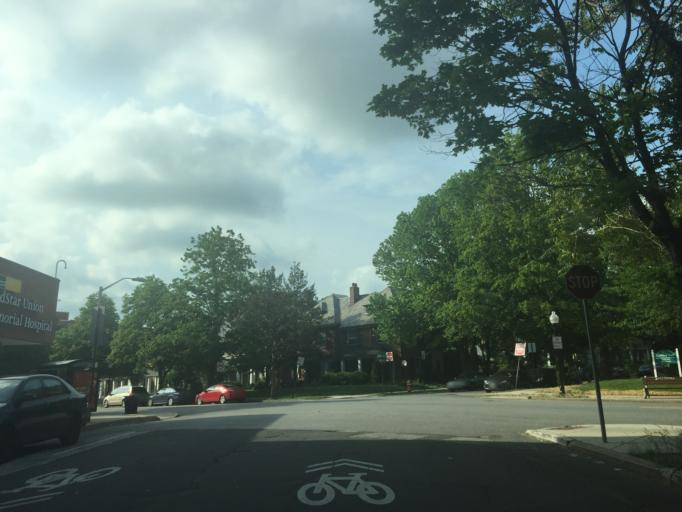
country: US
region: Maryland
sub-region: City of Baltimore
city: Baltimore
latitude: 39.3295
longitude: -76.6136
